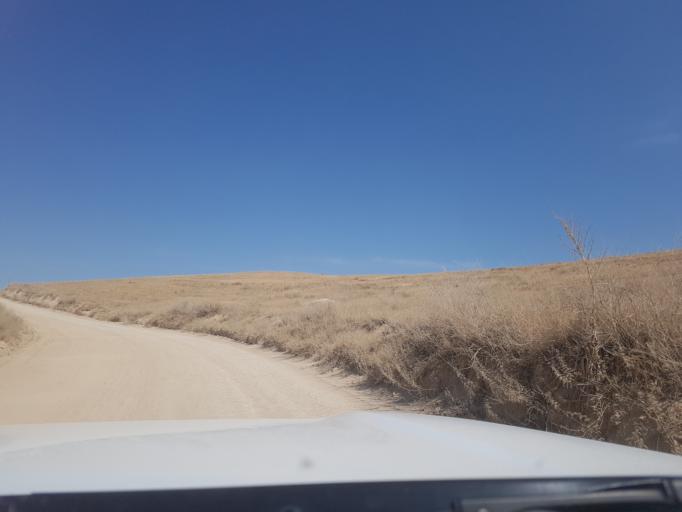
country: TM
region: Ahal
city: Baharly
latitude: 38.2707
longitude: 56.8952
